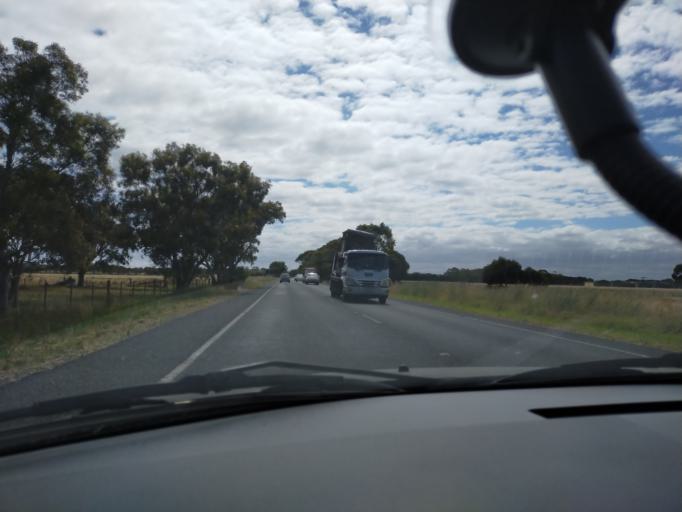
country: AU
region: Victoria
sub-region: Greater Geelong
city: Breakwater
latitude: -38.2562
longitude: 144.3976
